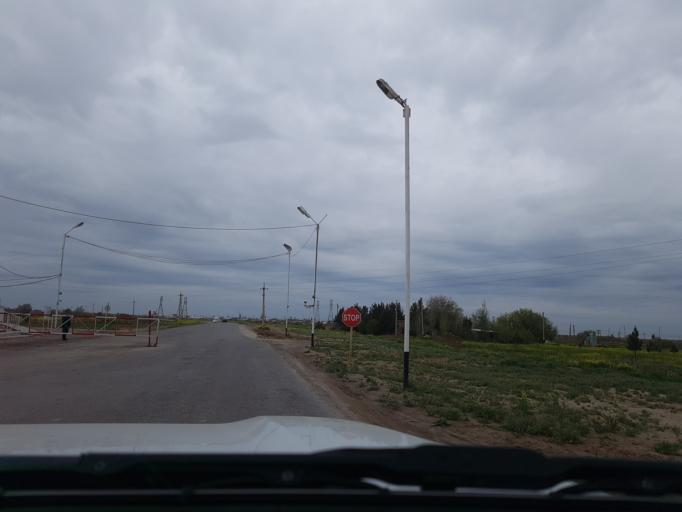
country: TM
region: Mary
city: Bayramaly
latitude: 37.7625
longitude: 62.5115
